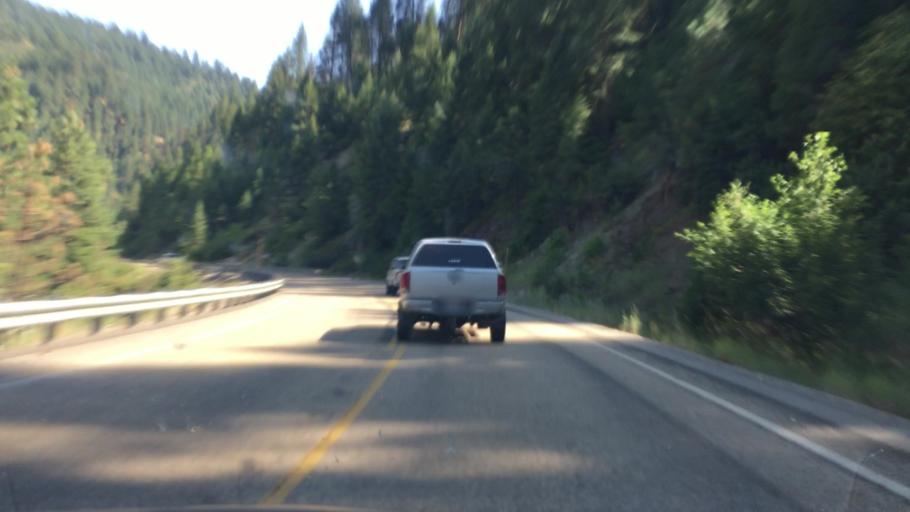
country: US
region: Idaho
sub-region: Valley County
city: Cascade
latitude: 44.1547
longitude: -116.1178
